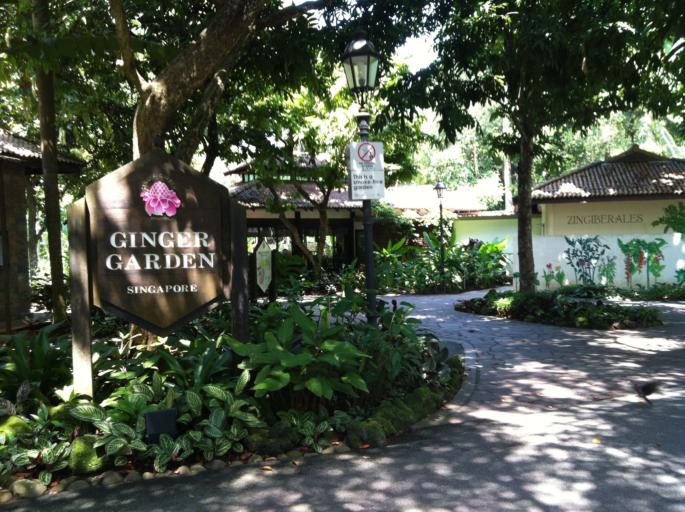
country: SG
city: Singapore
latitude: 1.3116
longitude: 103.8150
